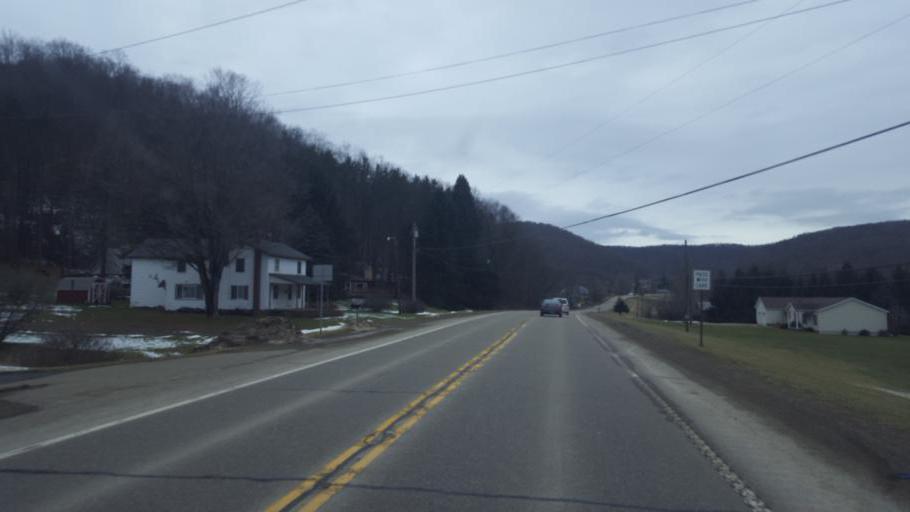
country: US
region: Pennsylvania
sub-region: Potter County
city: Coudersport
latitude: 41.8024
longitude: -78.0161
